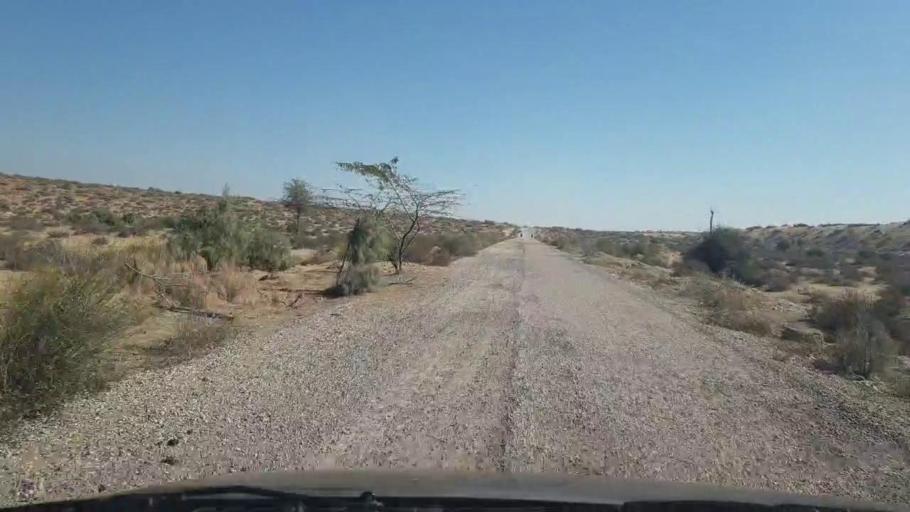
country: PK
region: Sindh
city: Bozdar
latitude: 27.0007
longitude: 68.8490
